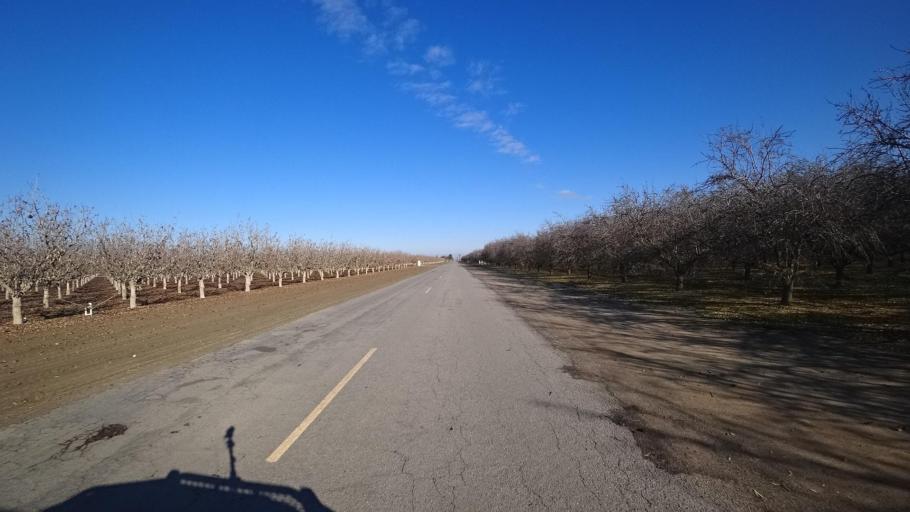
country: US
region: California
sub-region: Kern County
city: McFarland
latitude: 35.6983
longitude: -119.3118
